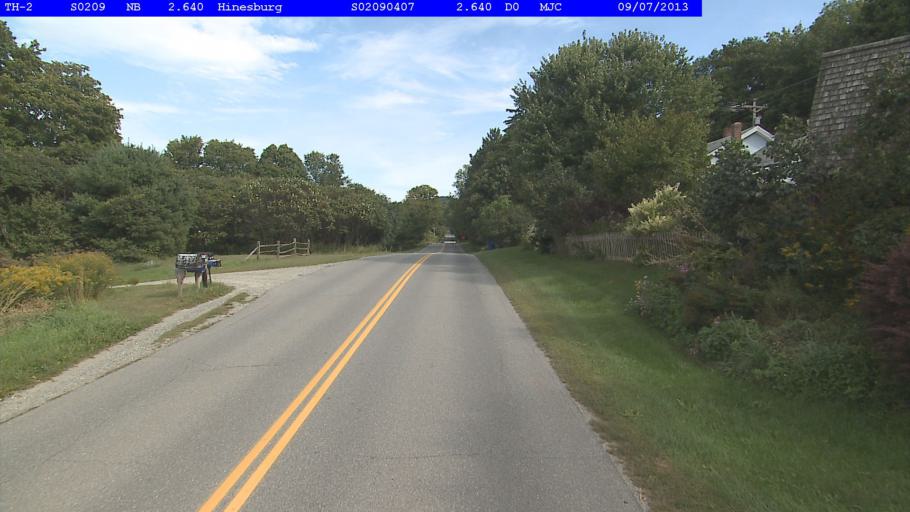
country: US
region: Vermont
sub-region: Chittenden County
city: Hinesburg
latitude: 44.3492
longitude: -73.0767
